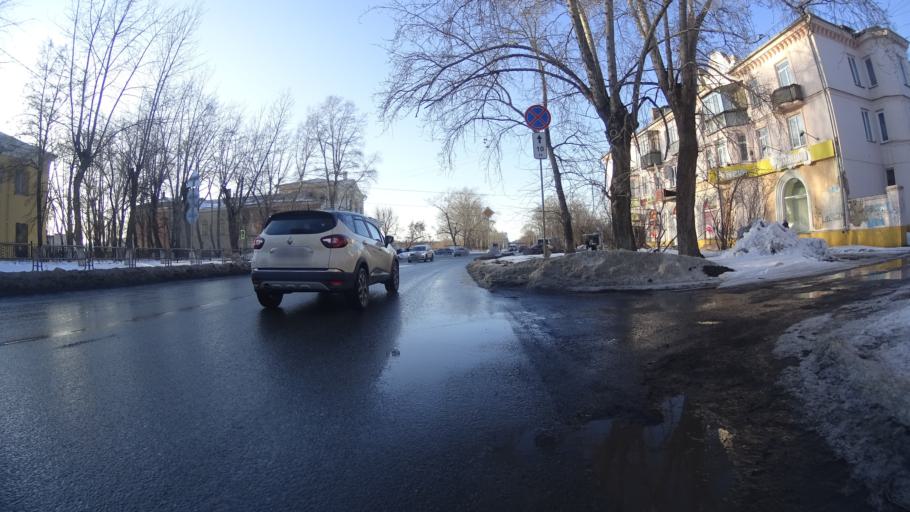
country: RU
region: Chelyabinsk
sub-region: Gorod Chelyabinsk
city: Chelyabinsk
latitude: 55.1300
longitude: 61.4652
